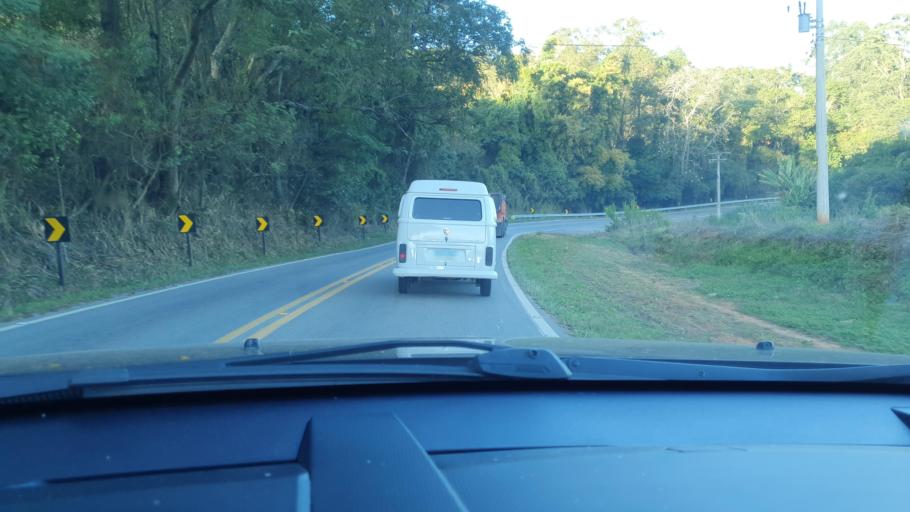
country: BR
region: Sao Paulo
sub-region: Piedade
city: Piedade
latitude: -23.7128
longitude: -47.3576
